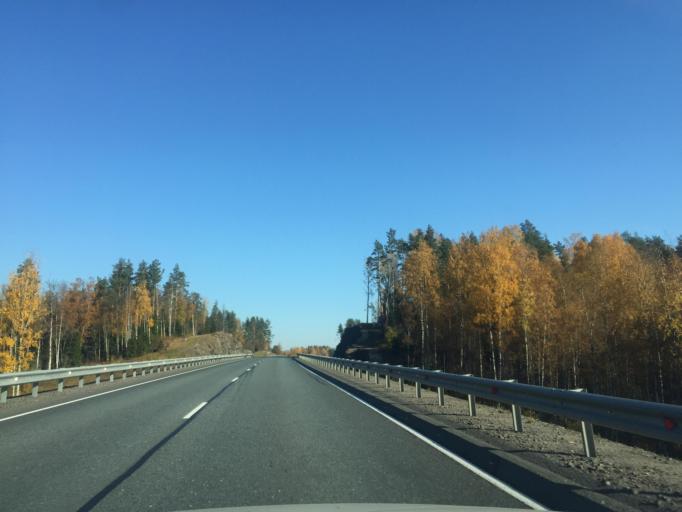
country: RU
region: Leningrad
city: Kuznechnoye
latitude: 61.3643
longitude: 29.8979
